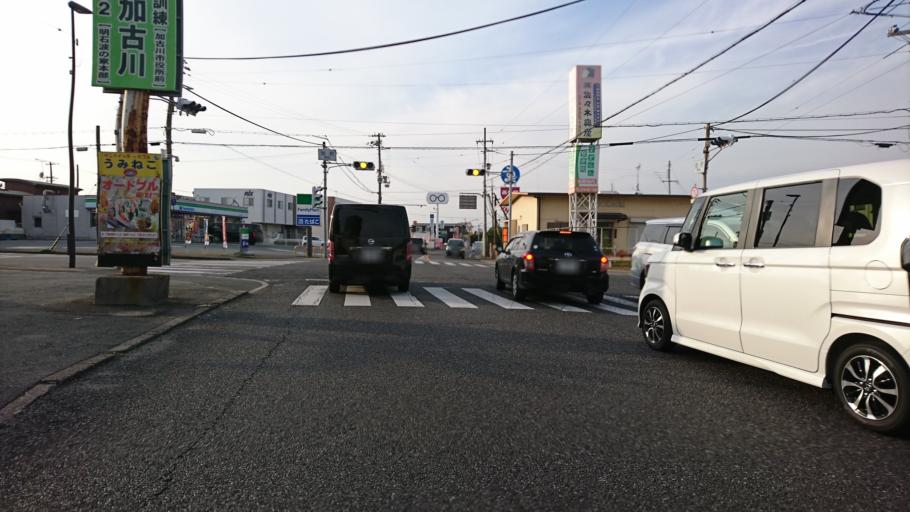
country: JP
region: Hyogo
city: Kakogawacho-honmachi
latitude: 34.7265
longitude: 134.8470
